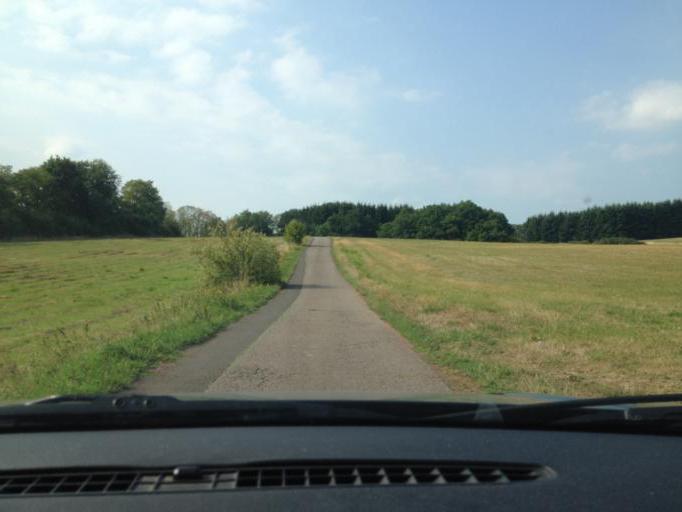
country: DE
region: Saarland
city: Namborn
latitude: 49.5500
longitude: 7.1333
